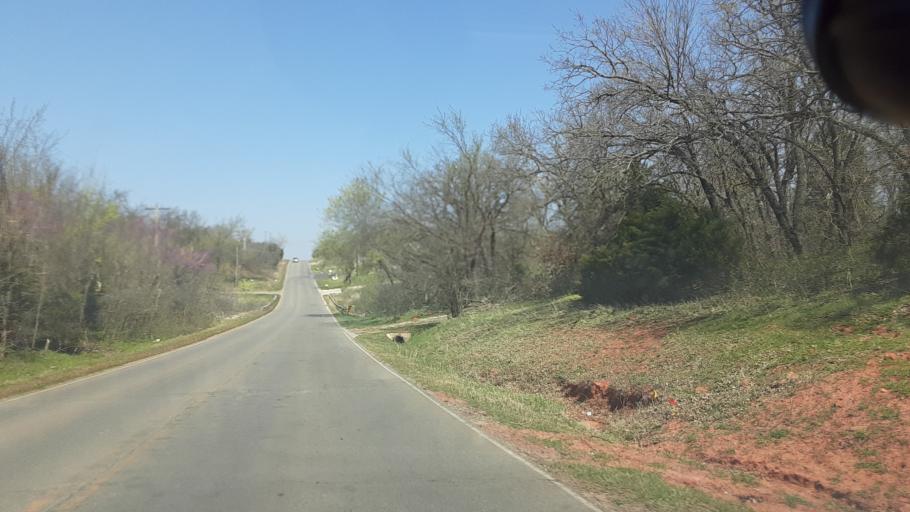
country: US
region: Oklahoma
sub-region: Oklahoma County
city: Edmond
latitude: 35.7457
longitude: -97.4784
